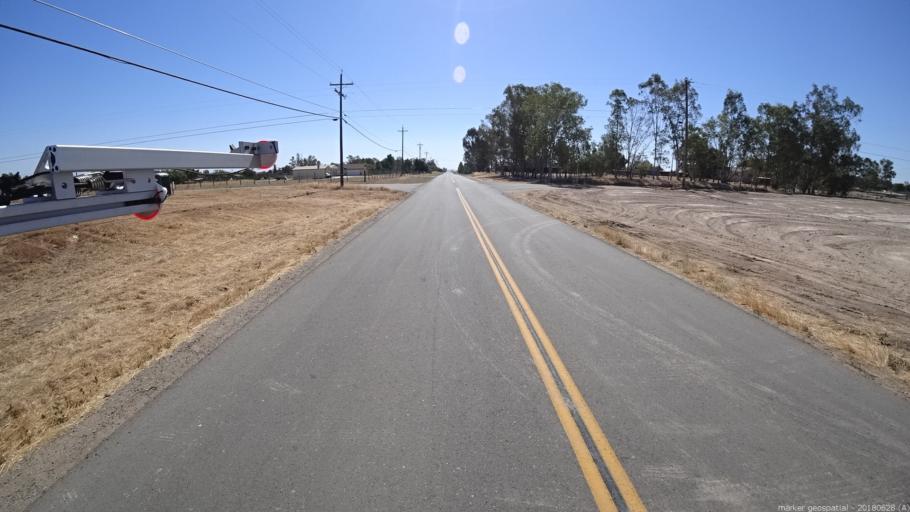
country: US
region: California
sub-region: Madera County
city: Bonadelle Ranchos-Madera Ranchos
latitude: 36.9958
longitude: -119.8906
